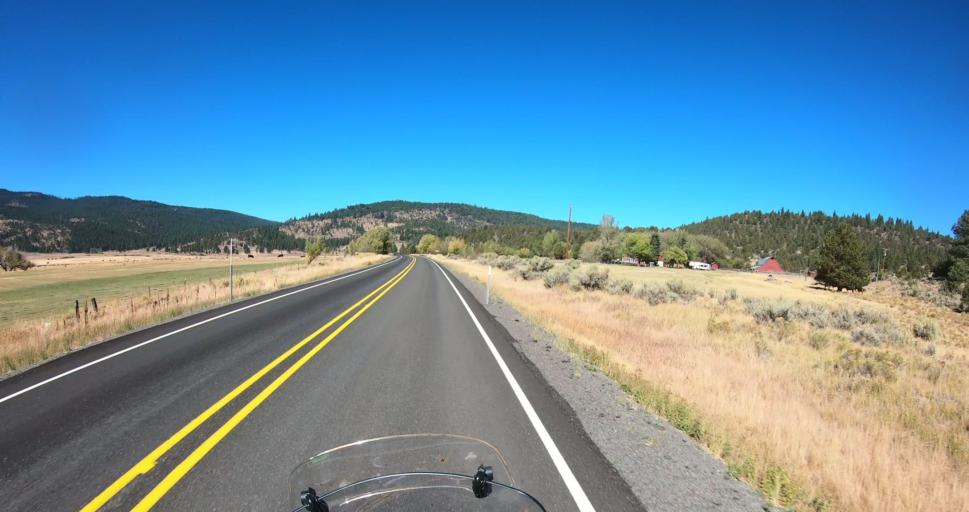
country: US
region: Oregon
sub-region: Lake County
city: Lakeview
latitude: 42.3776
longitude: -120.3001
